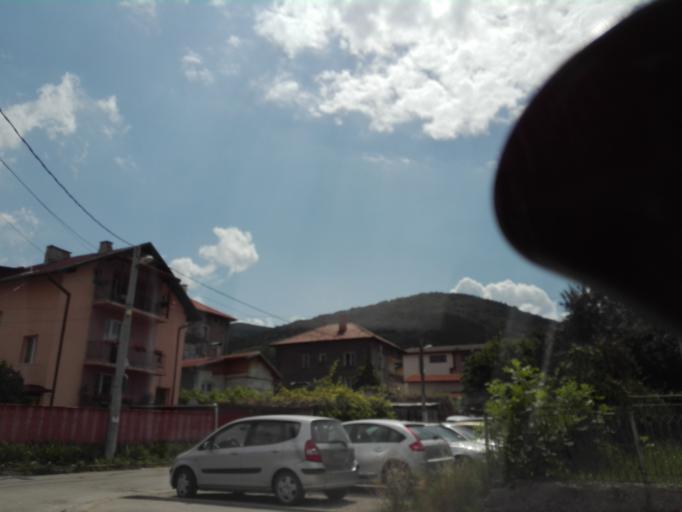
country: BG
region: Sofiya
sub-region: Obshtina Elin Pelin
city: Elin Pelin
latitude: 42.6023
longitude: 23.4785
